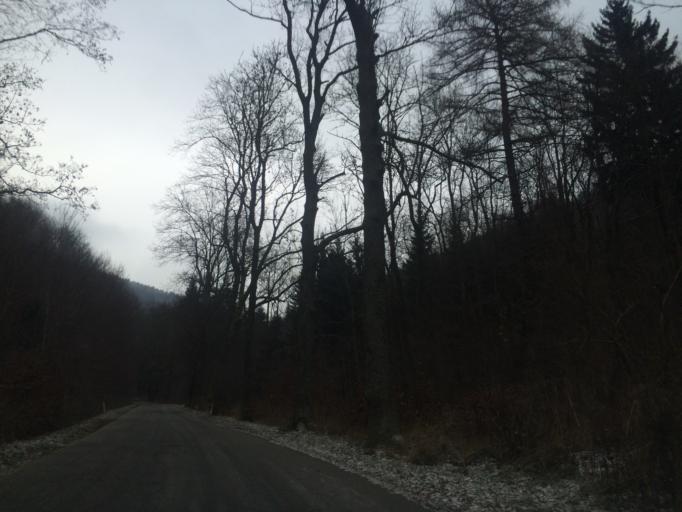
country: PL
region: Lower Silesian Voivodeship
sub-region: Powiat klodzki
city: Stronie Slaskie
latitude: 50.2673
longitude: 16.7645
